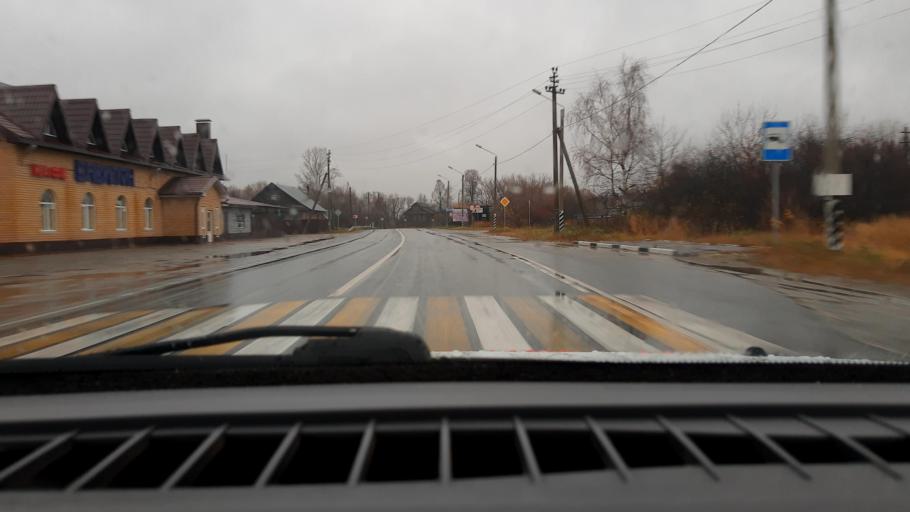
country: RU
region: Nizjnij Novgorod
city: Sitniki
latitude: 56.5429
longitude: 44.0193
